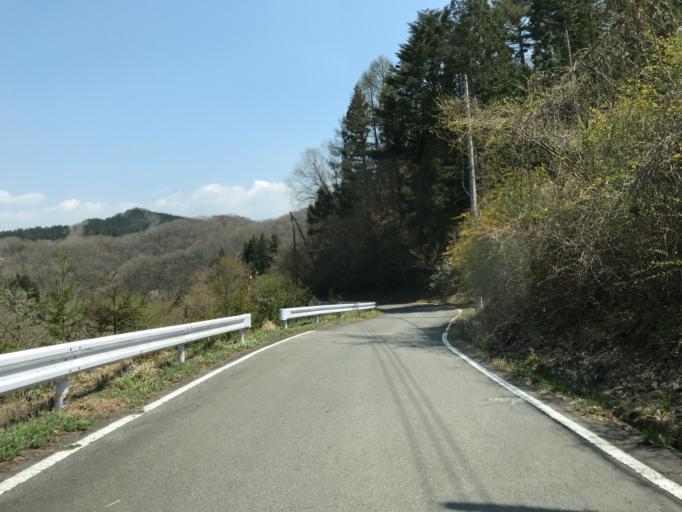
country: JP
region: Fukushima
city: Ishikawa
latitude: 36.9909
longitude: 140.6130
